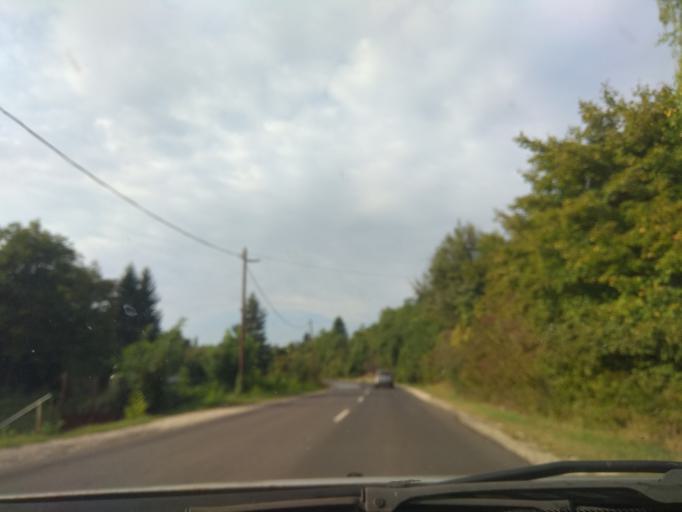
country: HU
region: Borsod-Abauj-Zemplen
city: Miskolc
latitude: 48.0888
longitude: 20.7530
